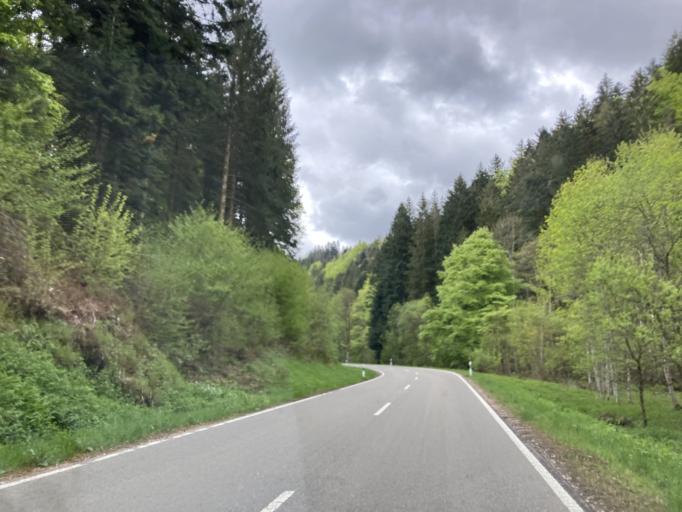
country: DE
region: Baden-Wuerttemberg
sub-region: Freiburg Region
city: Schonach im Schwarzwald
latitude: 48.1674
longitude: 8.1583
